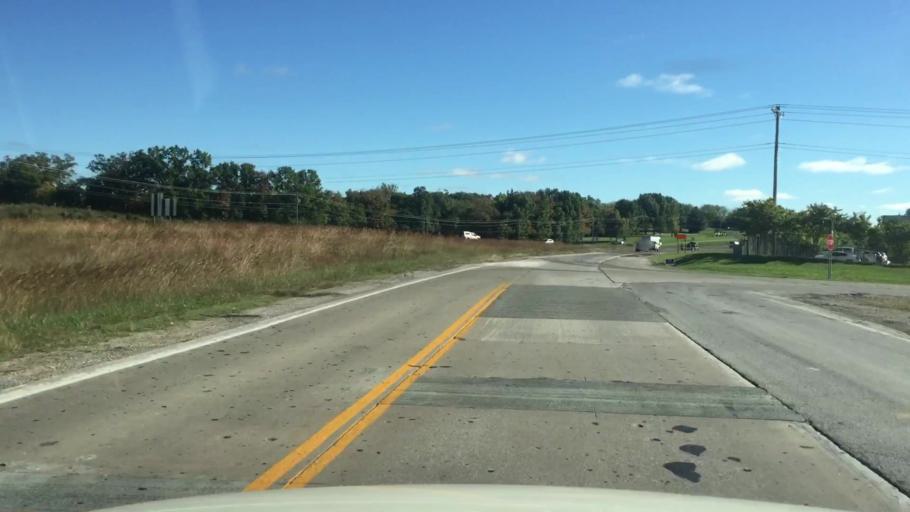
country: US
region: Missouri
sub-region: Boone County
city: Columbia
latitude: 38.9708
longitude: -92.4270
